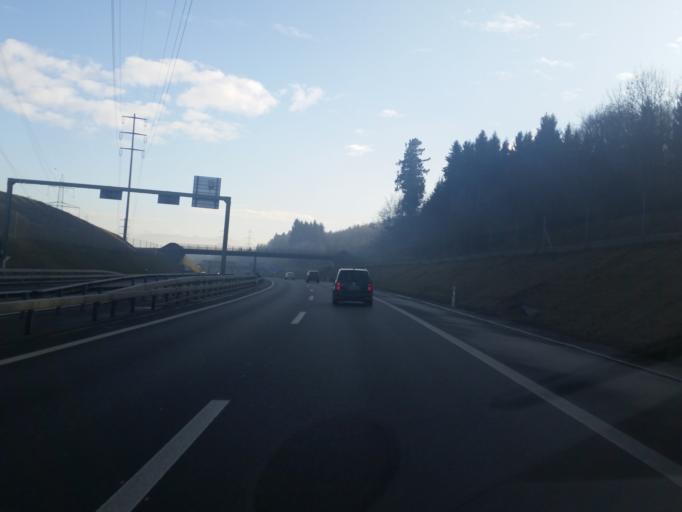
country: CH
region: Zurich
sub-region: Bezirk Affoltern
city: Ottenbach
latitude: 47.2851
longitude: 8.4240
